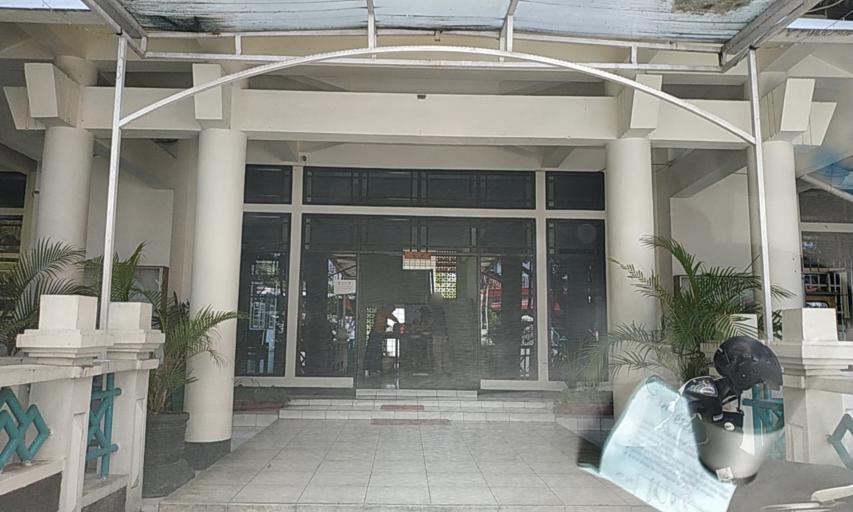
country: ID
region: Central Java
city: Selogiri
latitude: -7.8138
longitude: 110.9246
